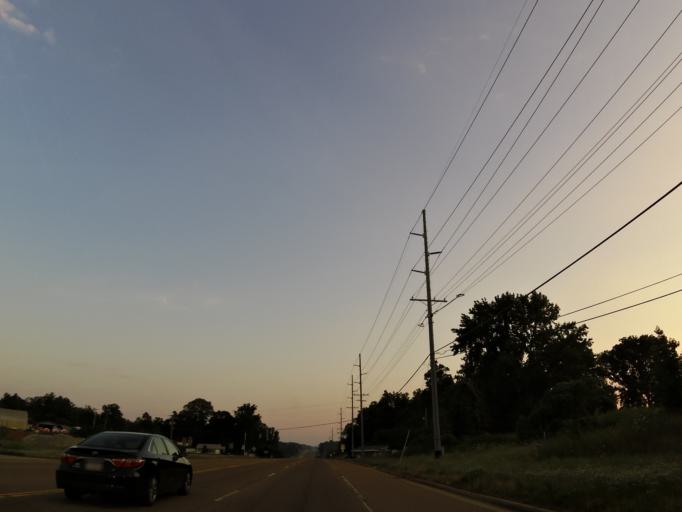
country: US
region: Tennessee
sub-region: Henry County
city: Paris
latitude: 36.2699
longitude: -88.3345
